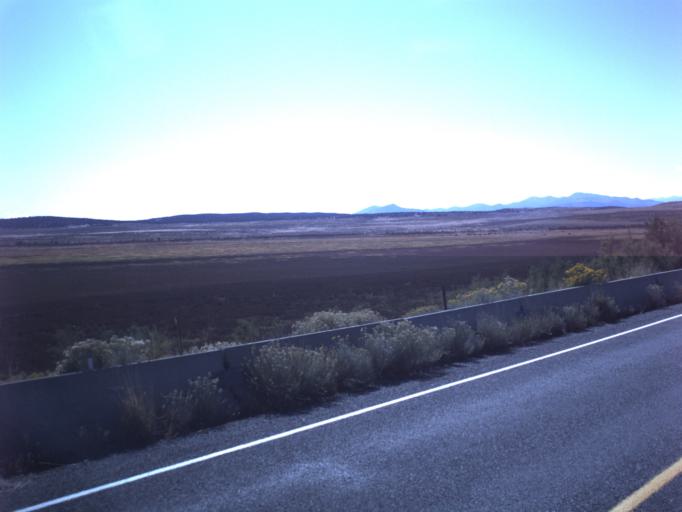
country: US
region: Utah
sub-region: Juab County
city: Nephi
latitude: 39.4921
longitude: -111.9659
